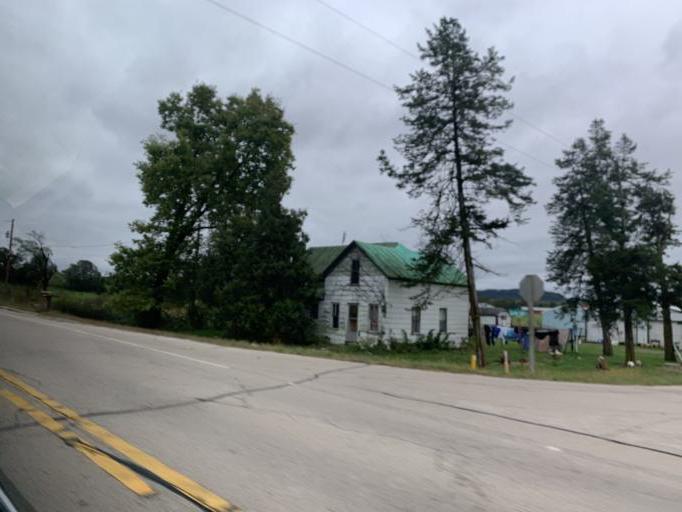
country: US
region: Wisconsin
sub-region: Grant County
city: Boscobel
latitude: 43.2054
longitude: -90.6121
